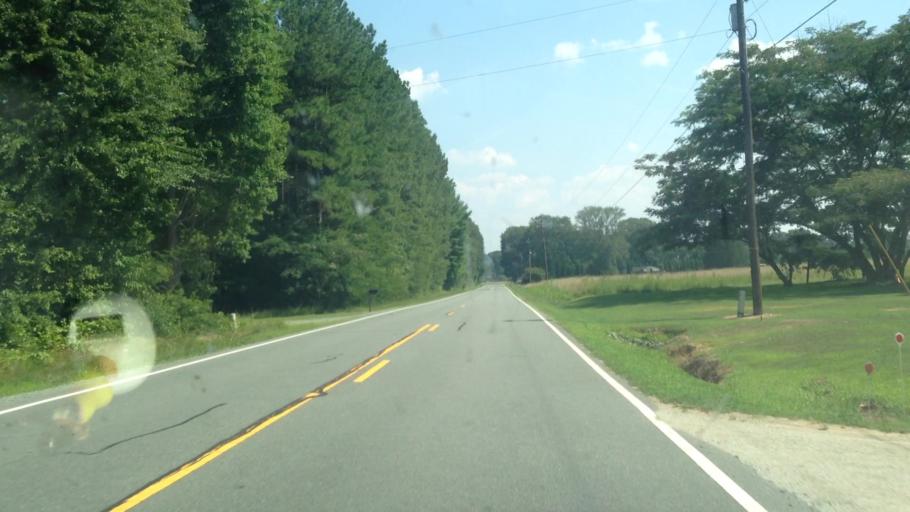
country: US
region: North Carolina
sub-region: Rockingham County
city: Madison
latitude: 36.3463
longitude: -80.0535
